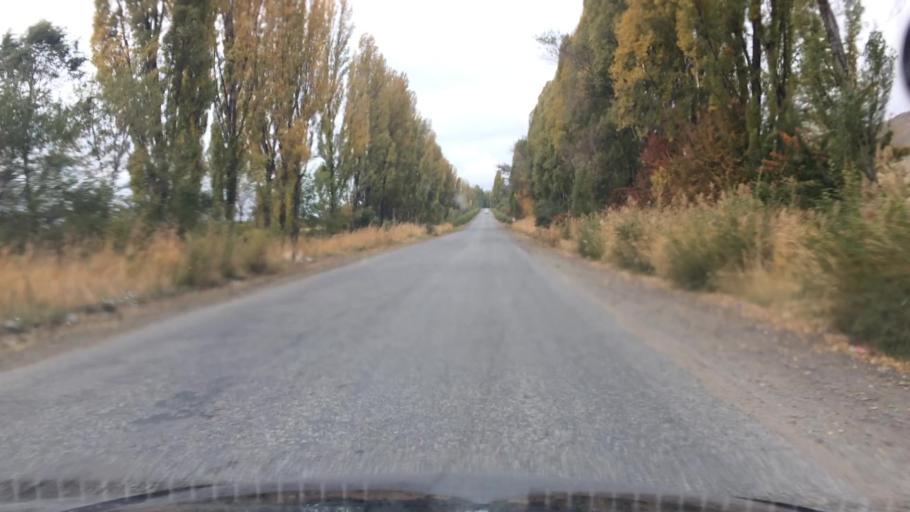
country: KG
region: Ysyk-Koel
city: Pokrovka
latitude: 42.7385
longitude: 77.8910
